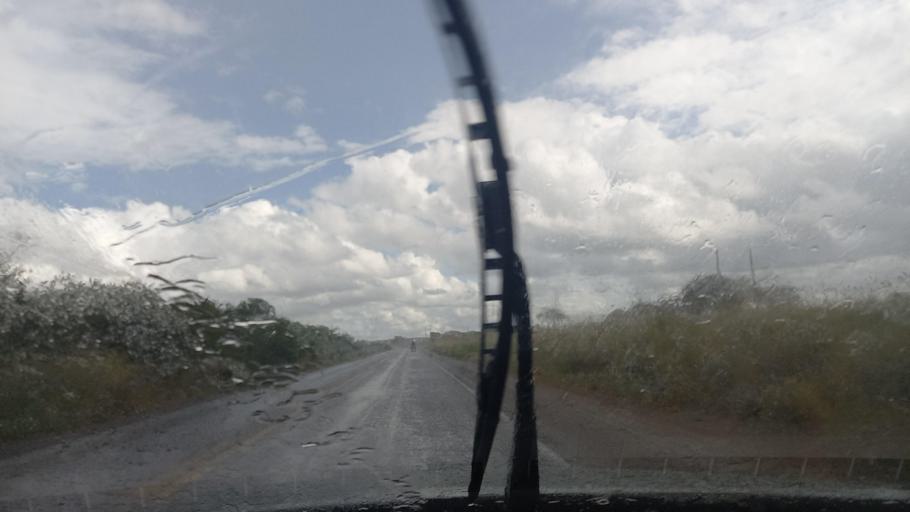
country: BR
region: Pernambuco
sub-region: Lajedo
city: Lajedo
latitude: -8.5765
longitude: -36.2855
